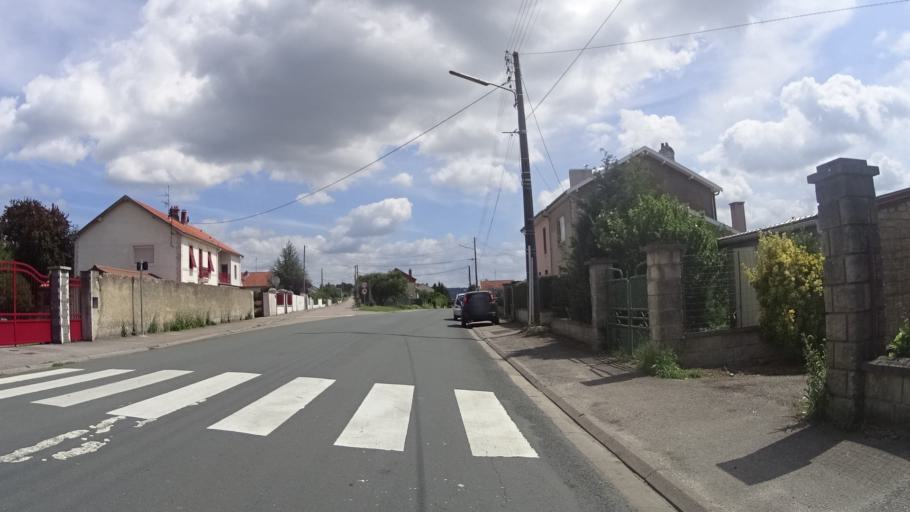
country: FR
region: Lorraine
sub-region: Departement de la Meuse
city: Euville
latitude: 48.7472
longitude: 5.6276
